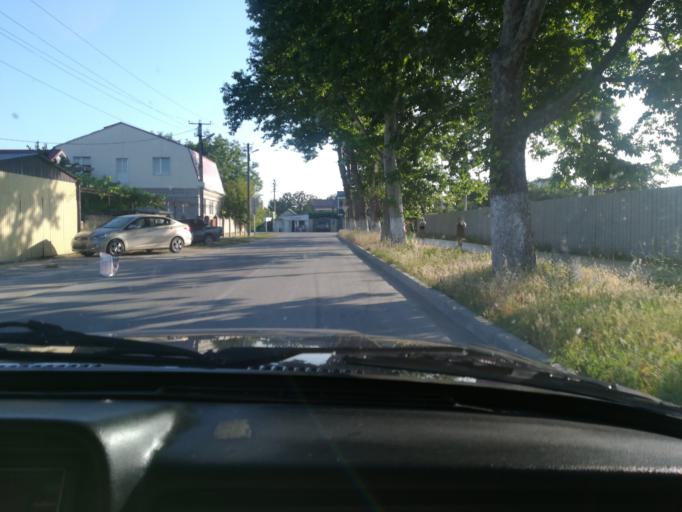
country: RU
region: Krasnodarskiy
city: Vityazevo
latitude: 45.0037
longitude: 37.2874
